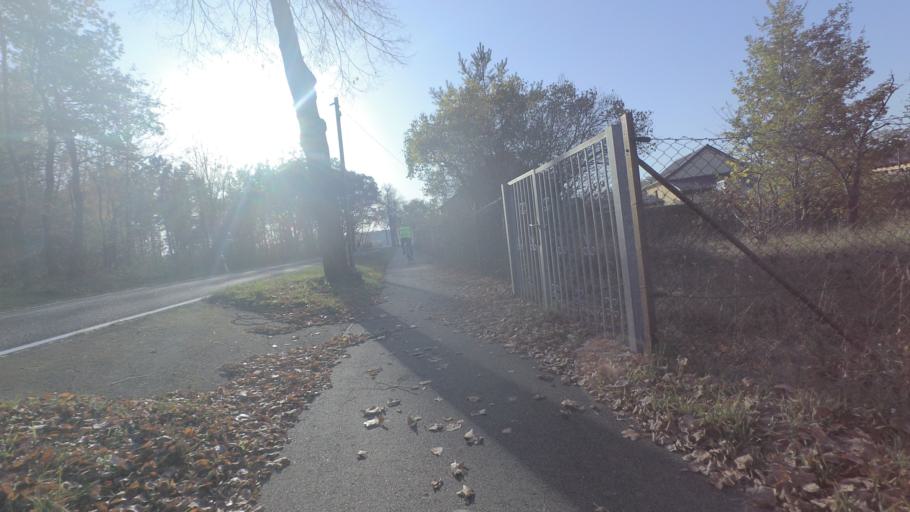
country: DE
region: Brandenburg
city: Sperenberg
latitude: 52.1626
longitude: 13.3571
